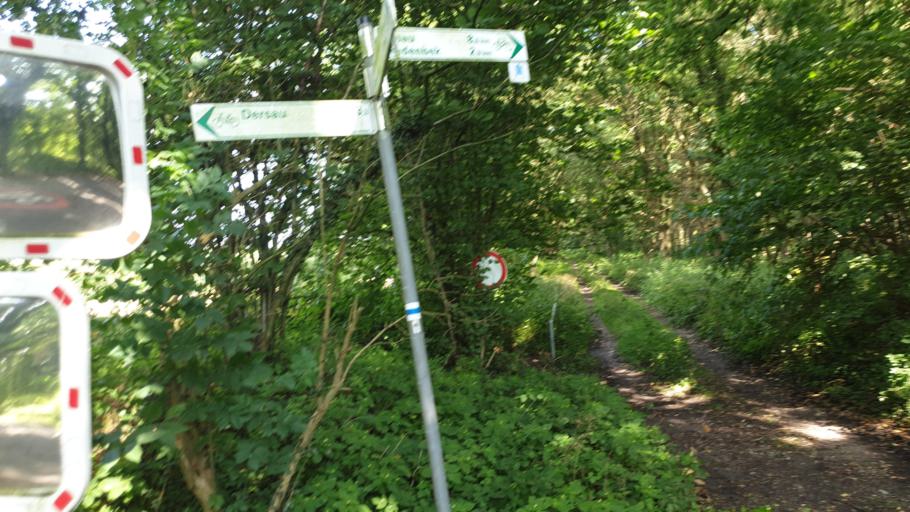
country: DE
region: Schleswig-Holstein
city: Stocksee
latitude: 54.0981
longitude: 10.3696
